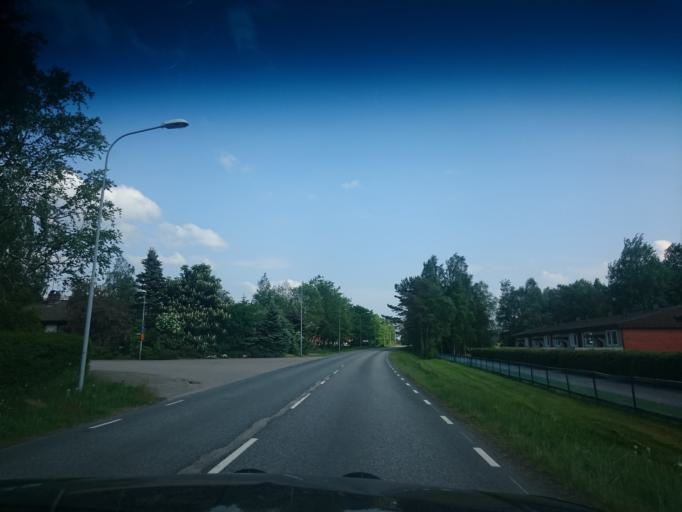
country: SE
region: Joenkoeping
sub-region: Vetlanda Kommun
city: Landsbro
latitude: 57.3825
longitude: 14.9676
